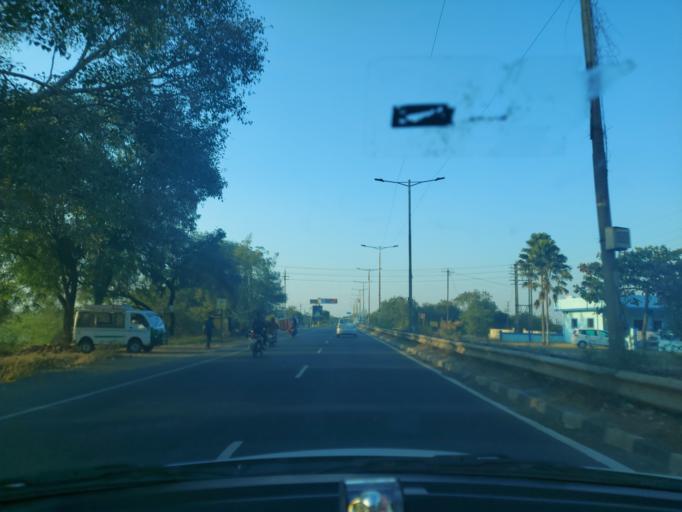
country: IN
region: Madhya Pradesh
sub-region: Ujjain
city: Ujjain
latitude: 23.1232
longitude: 75.7966
